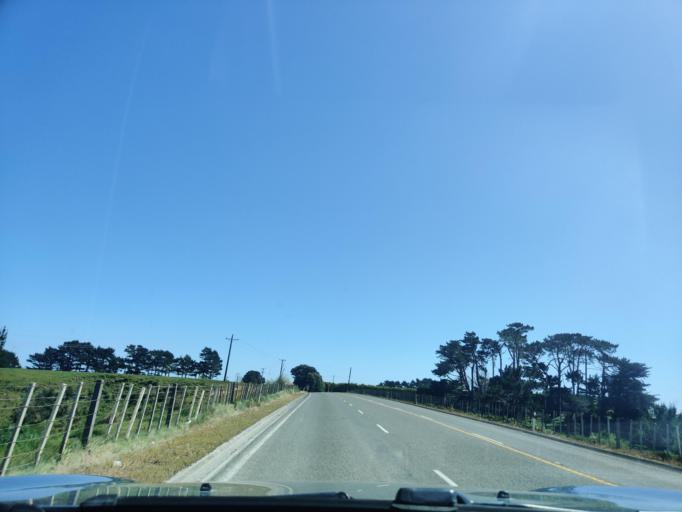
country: NZ
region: Taranaki
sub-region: South Taranaki District
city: Patea
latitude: -39.8020
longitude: 174.7244
